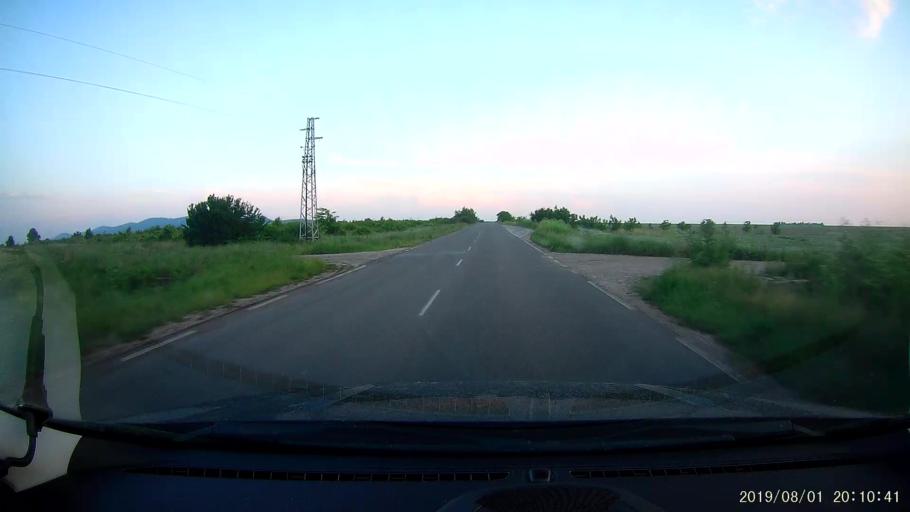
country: BG
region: Yambol
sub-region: Obshtina Yambol
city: Yambol
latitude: 42.4769
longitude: 26.6015
